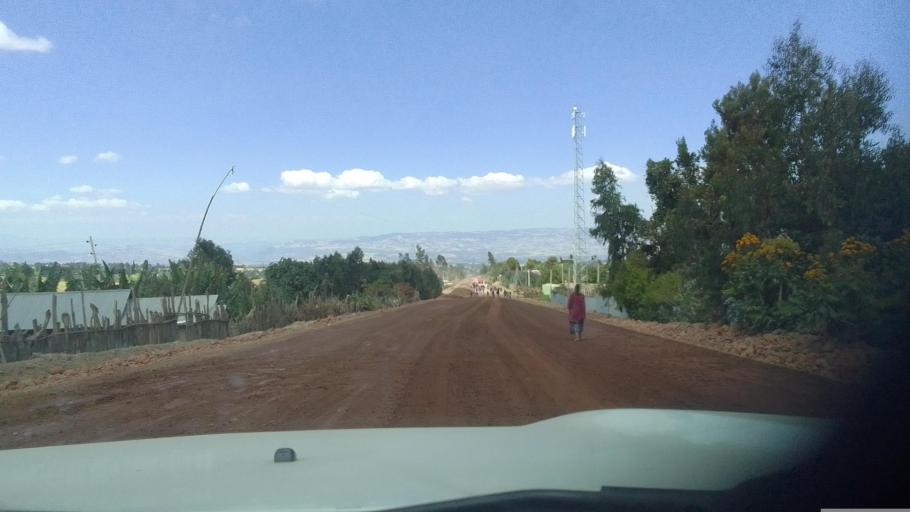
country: ET
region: Oromiya
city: Hagere Hiywet
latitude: 8.8537
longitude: 37.8932
